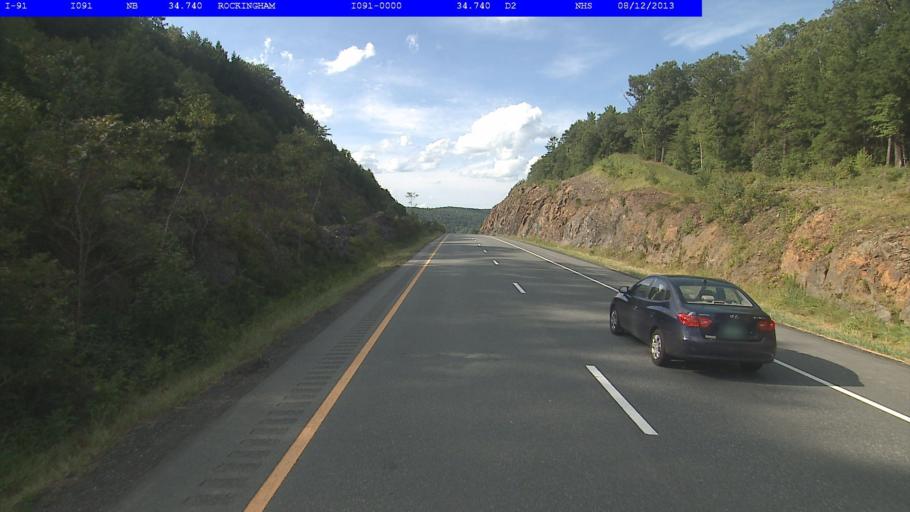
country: US
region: Vermont
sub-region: Windham County
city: Rockingham
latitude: 43.1720
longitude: -72.4624
